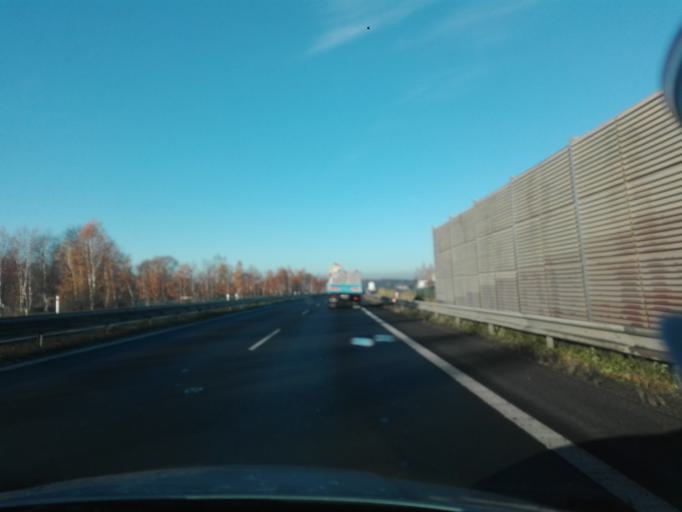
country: CZ
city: Dobra
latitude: 49.6759
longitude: 18.4179
